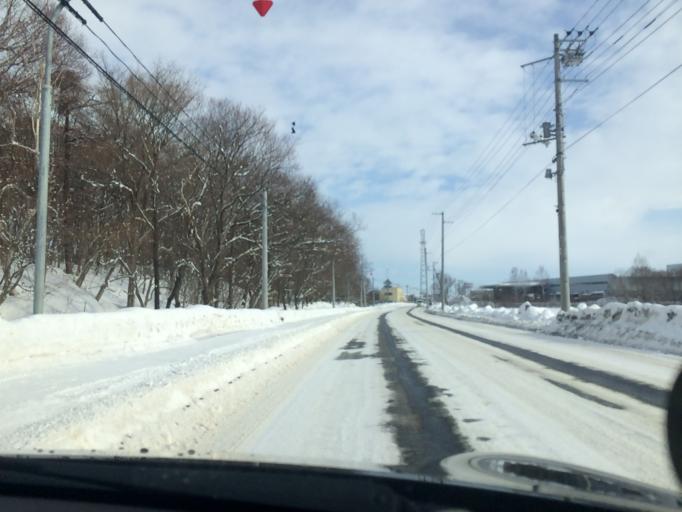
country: JP
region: Hokkaido
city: Kitahiroshima
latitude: 43.0072
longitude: 141.5547
